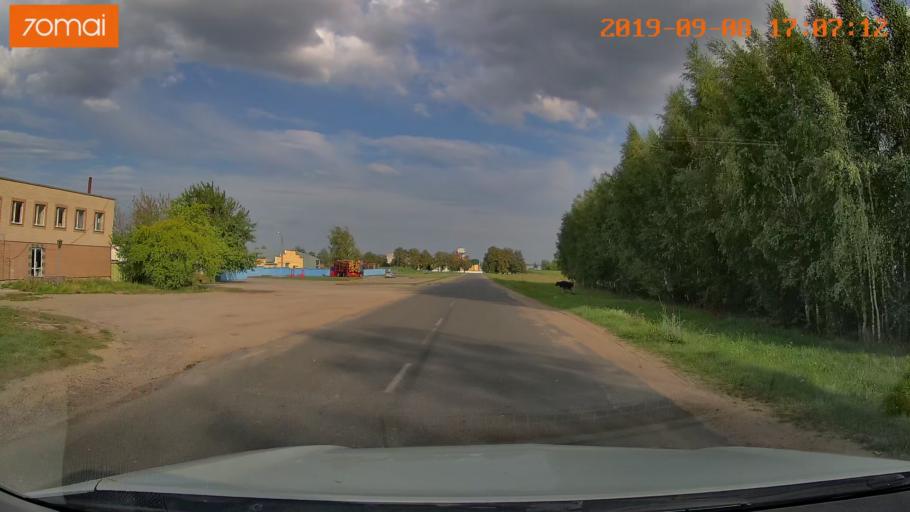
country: BY
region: Grodnenskaya
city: Hrodna
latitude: 53.6656
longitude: 23.9582
